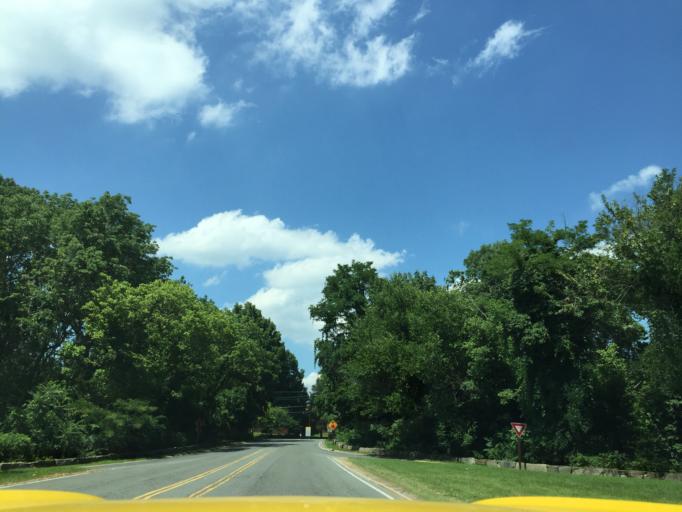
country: US
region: Maryland
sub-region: Montgomery County
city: Cabin John
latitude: 38.9715
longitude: -77.1528
